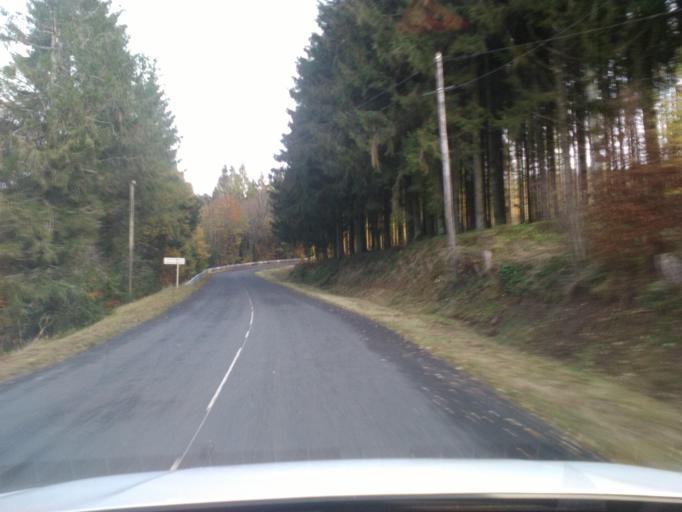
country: FR
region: Lorraine
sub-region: Departement des Vosges
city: Senones
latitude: 48.3887
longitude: 7.0945
